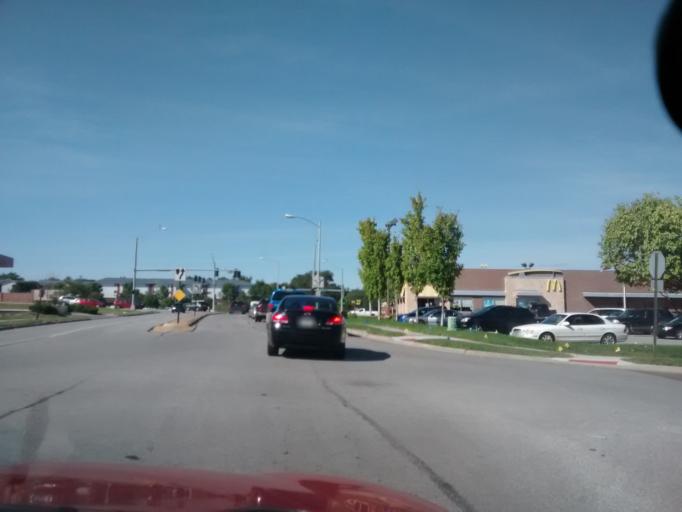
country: US
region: Nebraska
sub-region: Sarpy County
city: Offutt Air Force Base
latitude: 41.1581
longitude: -95.9425
